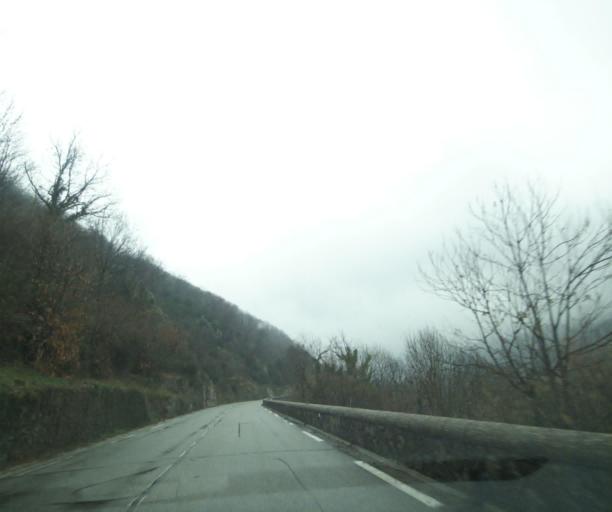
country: FR
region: Rhone-Alpes
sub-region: Departement de l'Ardeche
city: Thueyts
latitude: 44.6722
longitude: 4.1905
